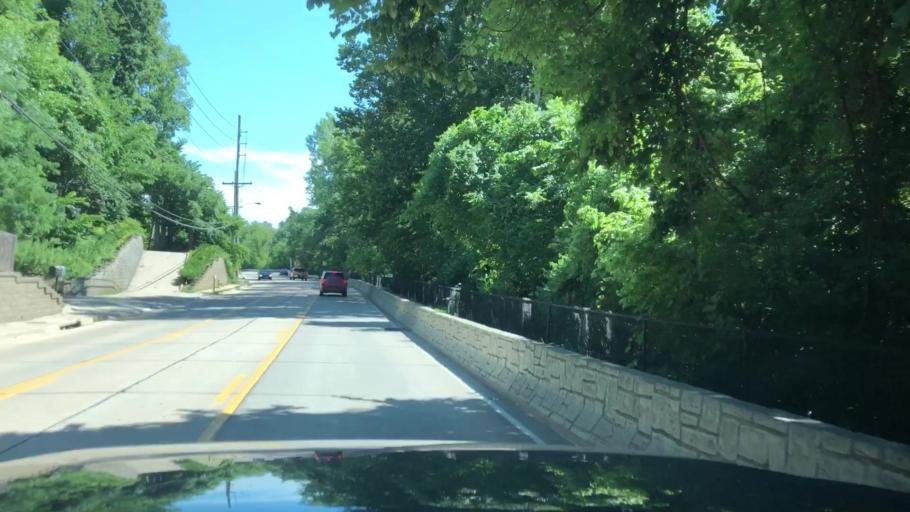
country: US
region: Missouri
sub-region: Saint Charles County
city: Saint Charles
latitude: 38.8122
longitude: -90.5129
